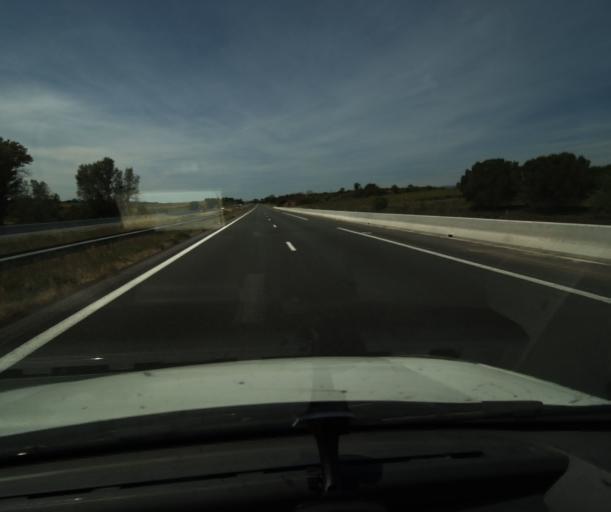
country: FR
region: Languedoc-Roussillon
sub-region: Departement de l'Aude
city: Trebes
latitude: 43.1854
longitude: 2.4713
